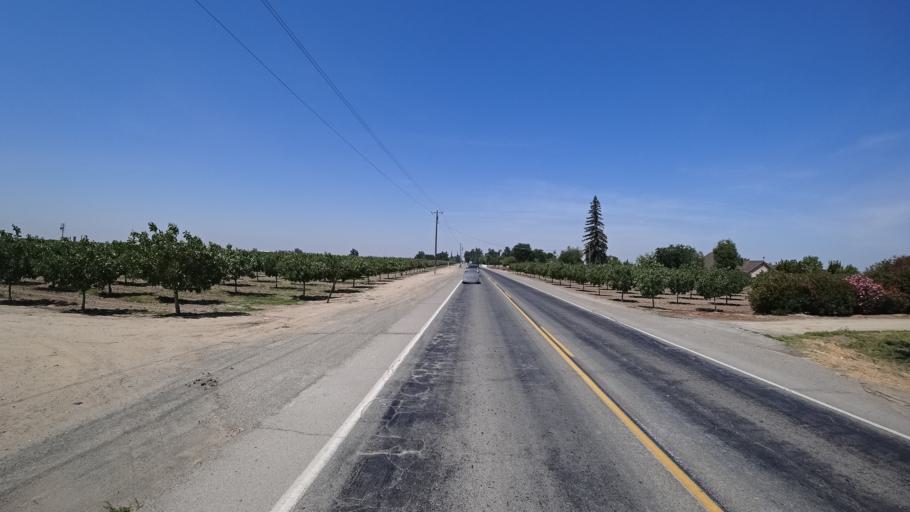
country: US
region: California
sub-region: Kings County
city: Lucerne
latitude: 36.4011
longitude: -119.6744
